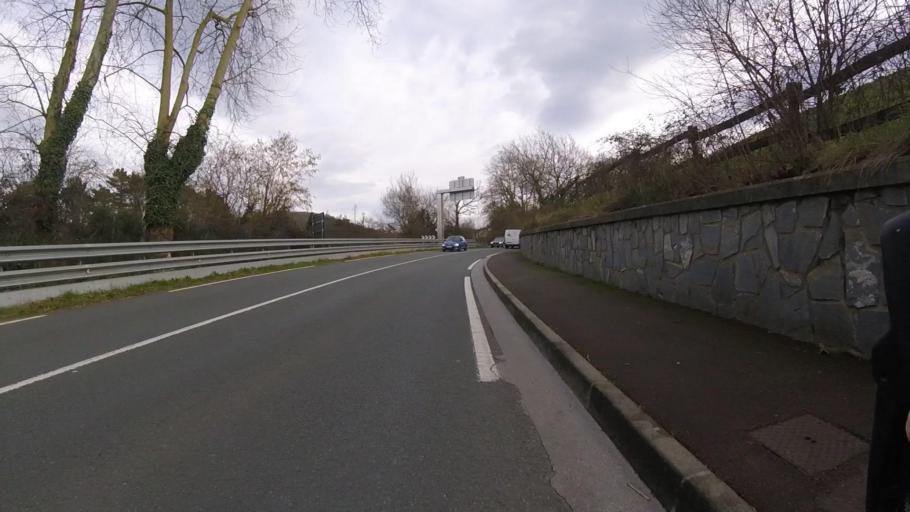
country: ES
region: Basque Country
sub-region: Provincia de Guipuzcoa
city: Lezo
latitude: 43.3051
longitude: -1.8769
